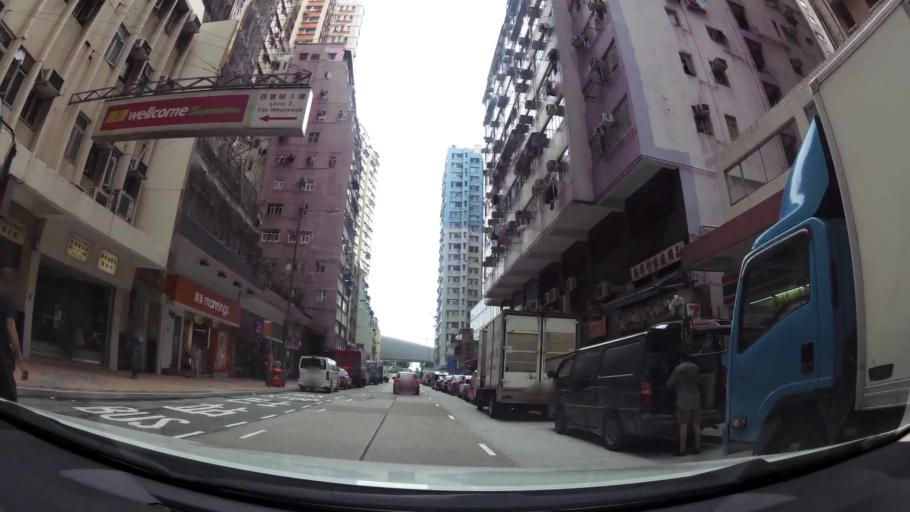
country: HK
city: Hong Kong
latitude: 22.2864
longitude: 114.1337
